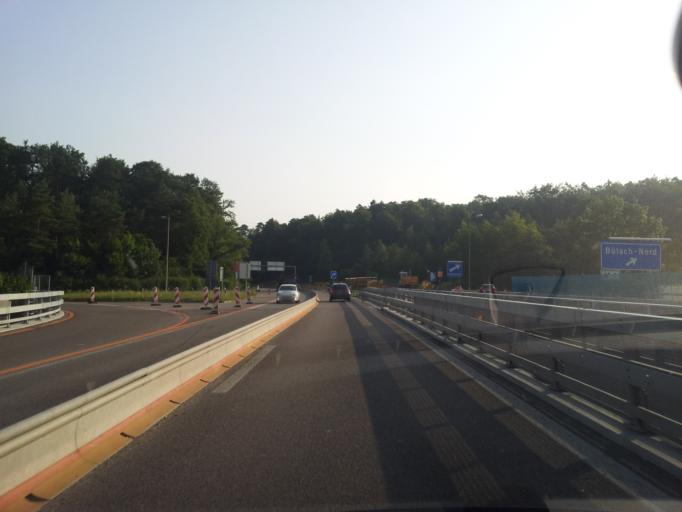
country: CH
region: Zurich
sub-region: Bezirk Buelach
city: Buelach / Soligaenter
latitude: 47.5291
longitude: 8.5330
